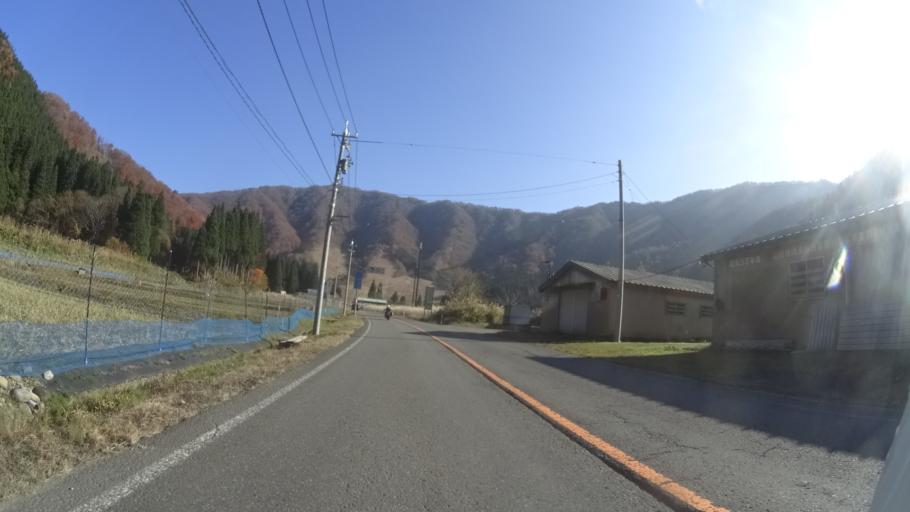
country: JP
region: Fukui
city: Ono
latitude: 35.9029
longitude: 136.6492
